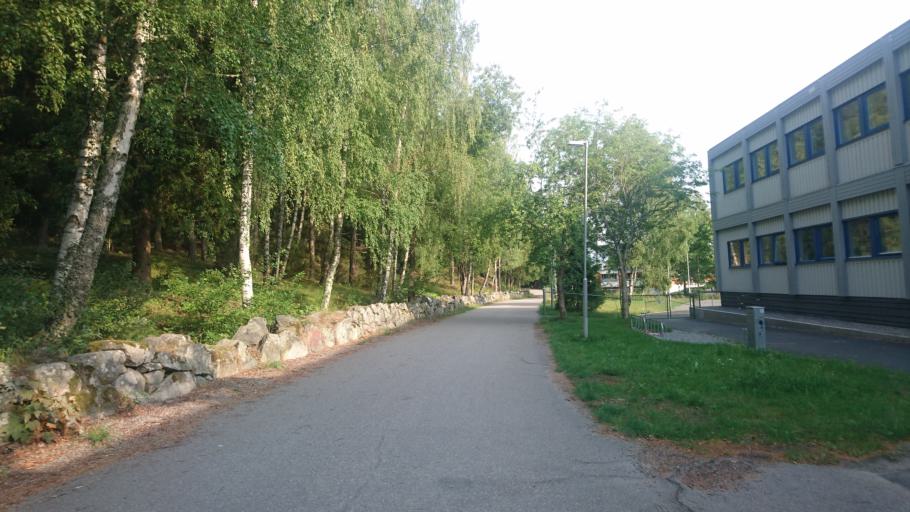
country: SE
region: Stockholm
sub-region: Upplands Vasby Kommun
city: Upplands Vaesby
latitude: 59.5113
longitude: 17.9141
